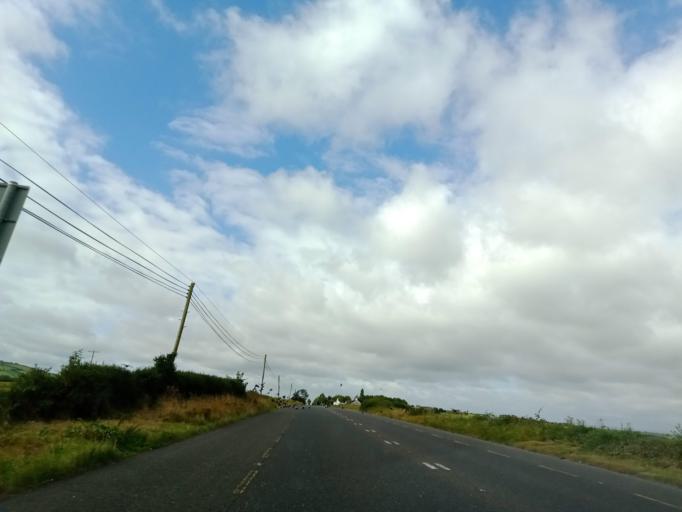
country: IE
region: Leinster
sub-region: Laois
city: Abbeyleix
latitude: 52.8269
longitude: -7.4577
